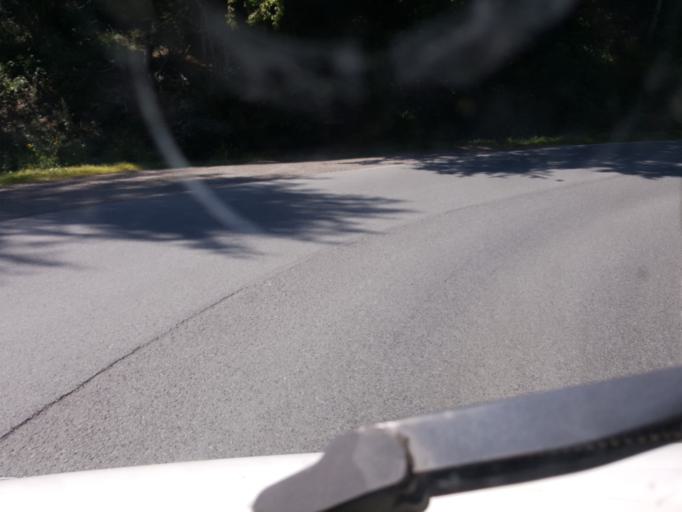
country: DE
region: North Rhine-Westphalia
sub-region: Regierungsbezirk Detmold
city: Hille
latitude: 52.2725
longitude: 8.7745
